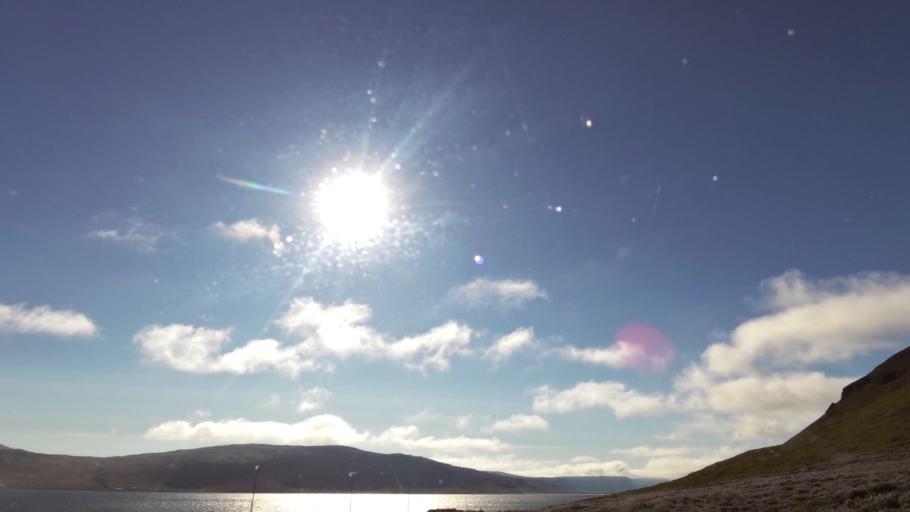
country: IS
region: West
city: Olafsvik
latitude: 65.5434
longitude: -23.8763
